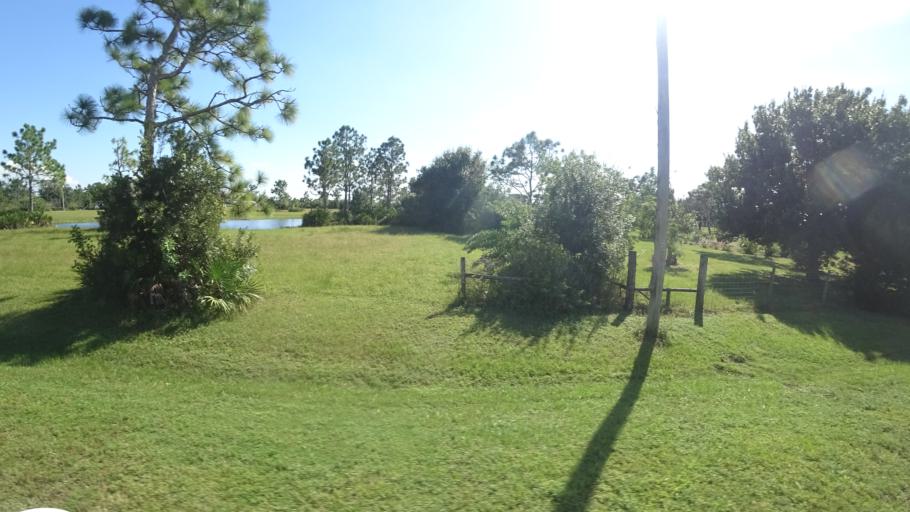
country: US
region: Florida
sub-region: Sarasota County
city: The Meadows
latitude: 27.4306
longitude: -82.2847
